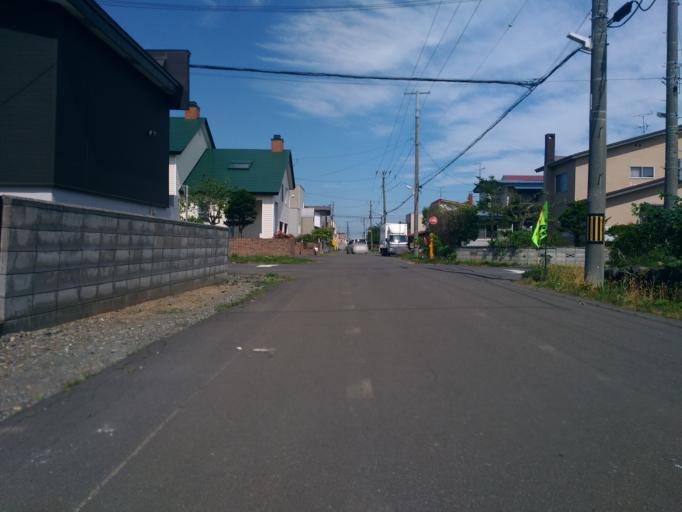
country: JP
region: Hokkaido
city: Ebetsu
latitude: 43.0805
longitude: 141.5088
